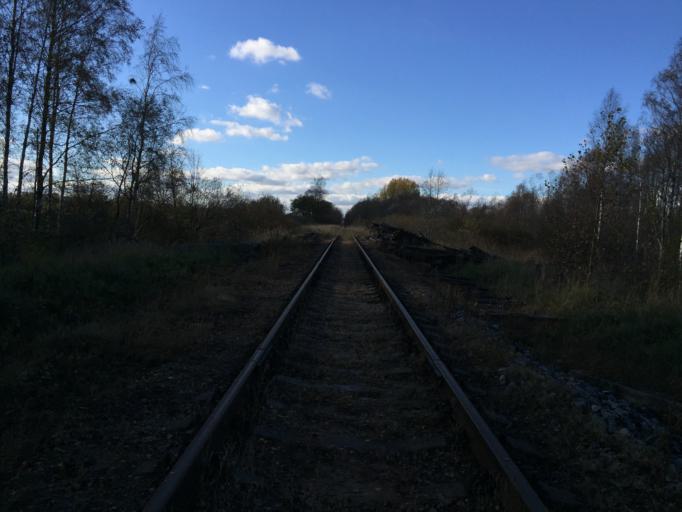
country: LV
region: Tukuma Rajons
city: Tukums
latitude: 56.9600
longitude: 23.1044
